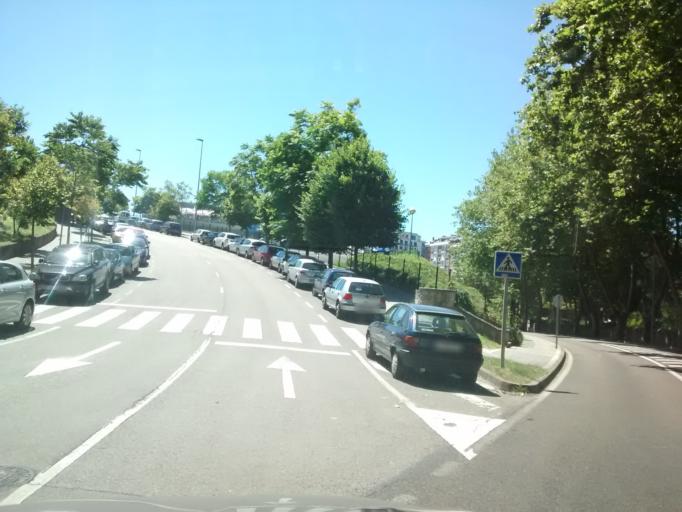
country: ES
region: Cantabria
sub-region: Provincia de Cantabria
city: Santander
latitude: 43.4838
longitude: -3.7894
